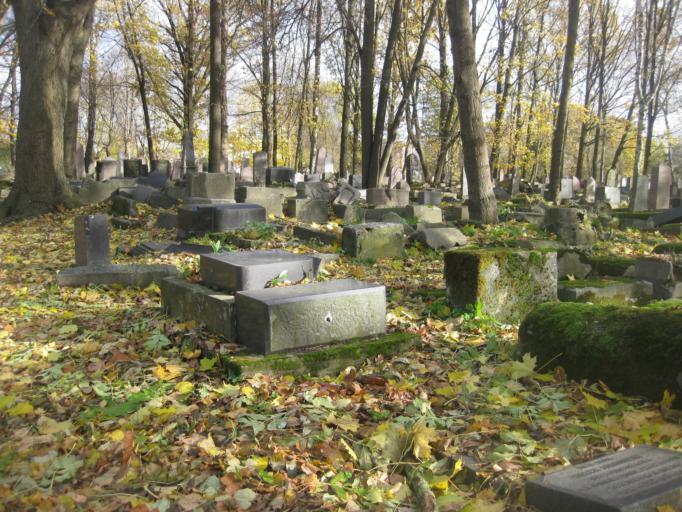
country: LT
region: Kauno apskritis
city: Dainava (Kaunas)
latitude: 54.9083
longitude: 23.9445
